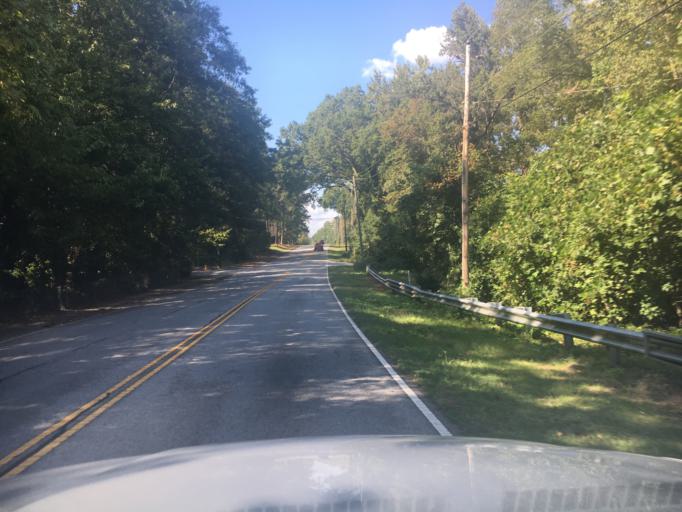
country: US
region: South Carolina
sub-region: Greenwood County
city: Greenwood
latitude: 34.2075
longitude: -82.1646
